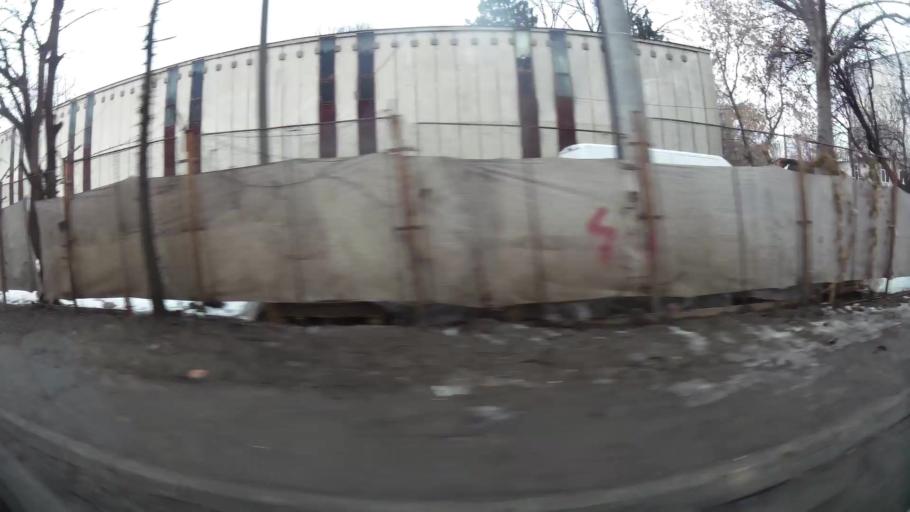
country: RO
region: Ilfov
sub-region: Comuna Popesti-Leordeni
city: Popesti-Leordeni
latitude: 44.4036
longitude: 26.1497
